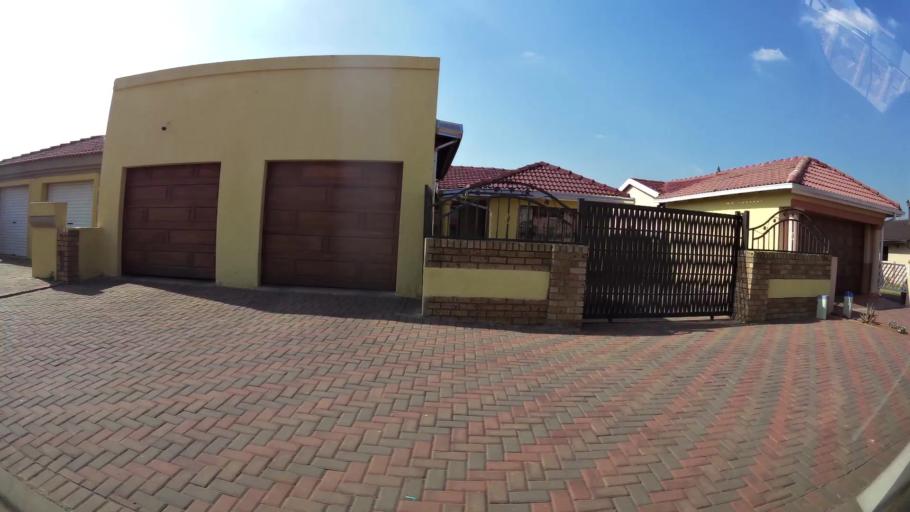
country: ZA
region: Gauteng
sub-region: Ekurhuleni Metropolitan Municipality
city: Benoni
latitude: -26.1423
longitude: 28.4089
